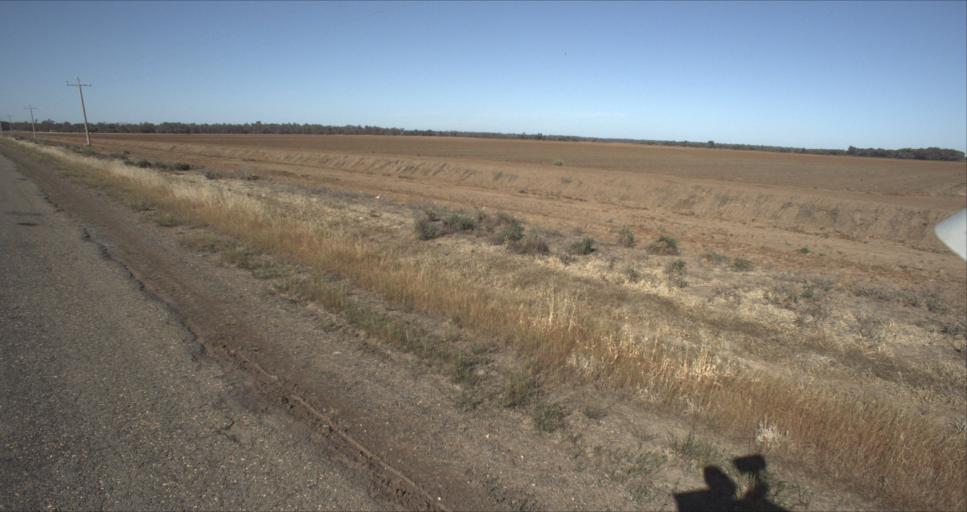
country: AU
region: New South Wales
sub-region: Leeton
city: Leeton
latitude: -34.5959
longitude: 146.2587
